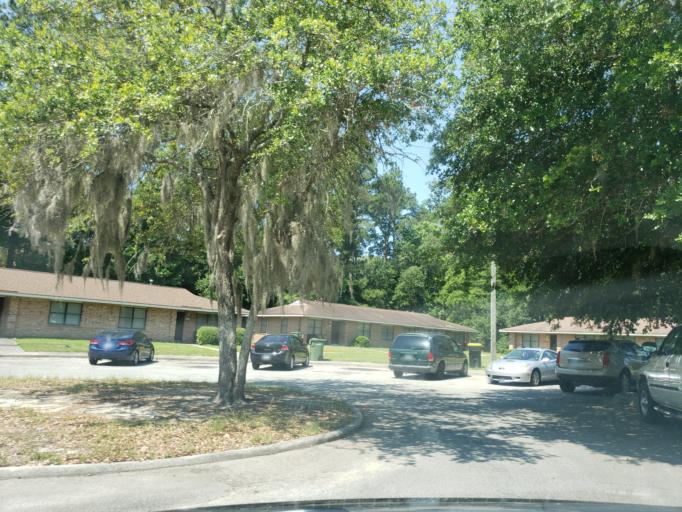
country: US
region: Georgia
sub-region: Chatham County
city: Montgomery
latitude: 31.9947
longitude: -81.1352
